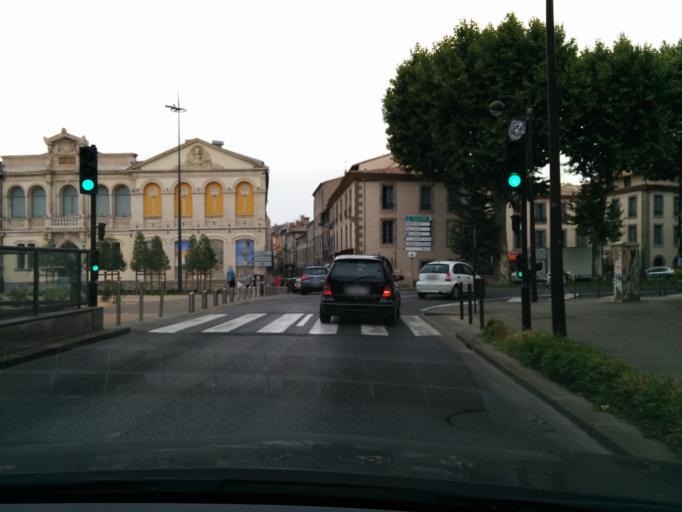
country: FR
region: Languedoc-Roussillon
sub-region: Departement de l'Aude
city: Carcassonne
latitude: 43.2126
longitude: 2.3560
